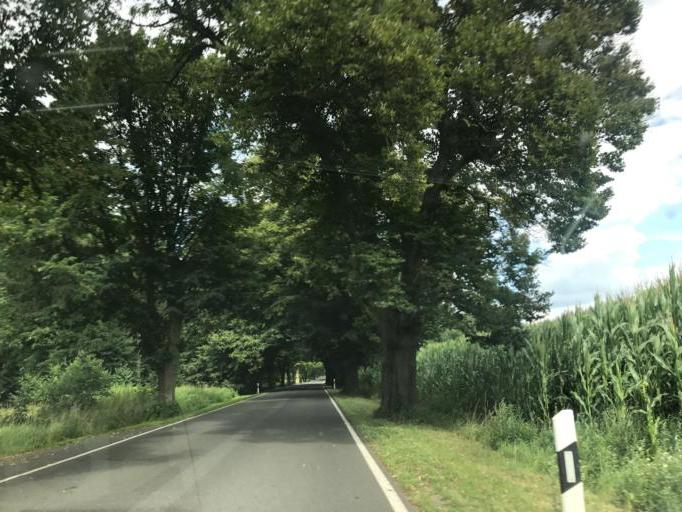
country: DE
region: Mecklenburg-Vorpommern
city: Wesenberg
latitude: 53.2047
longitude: 12.9130
